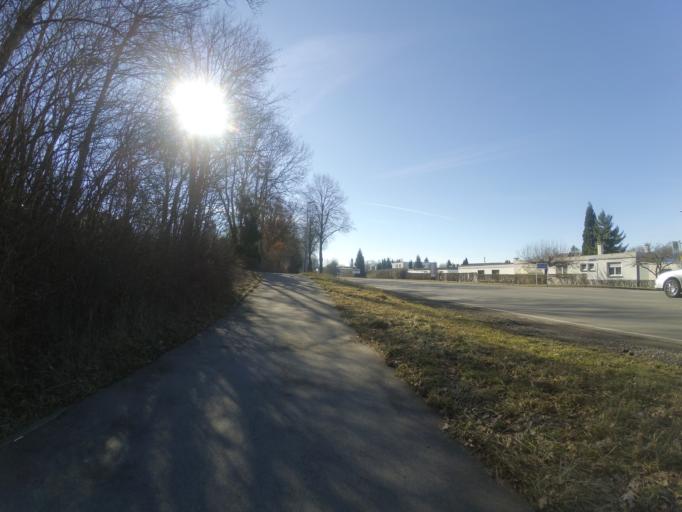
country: DE
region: Baden-Wuerttemberg
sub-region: Tuebingen Region
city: Laupheim
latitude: 48.2393
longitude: 9.8834
